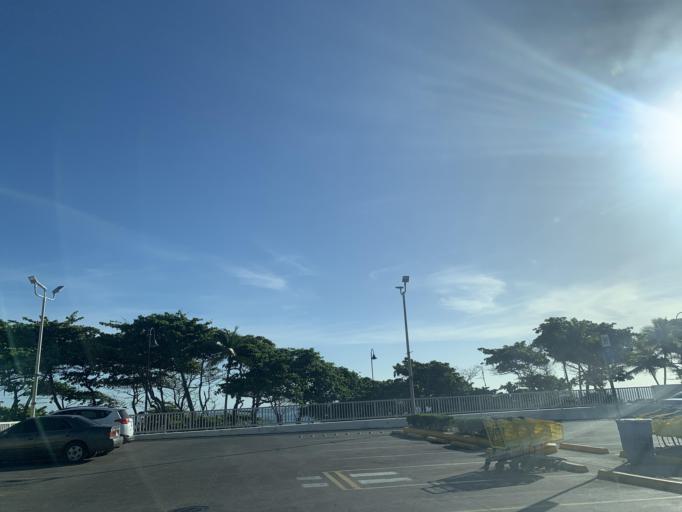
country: DO
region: Puerto Plata
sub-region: Puerto Plata
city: Puerto Plata
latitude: 19.7955
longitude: -70.6842
